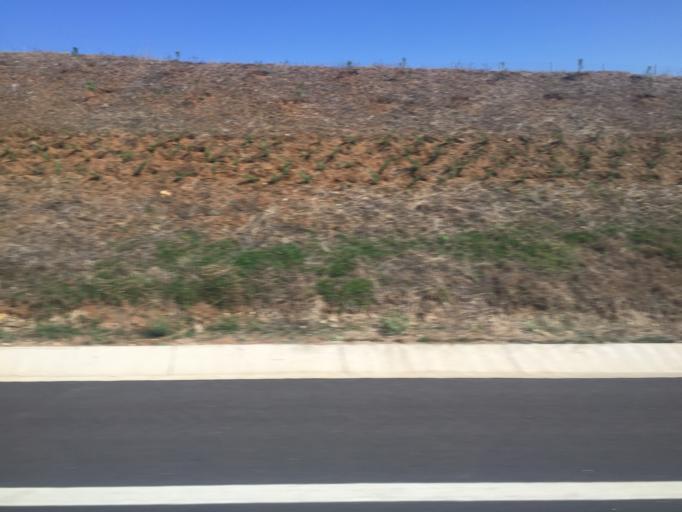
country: TR
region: Bursa
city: Mahmudiye
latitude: 40.2705
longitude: 28.6221
